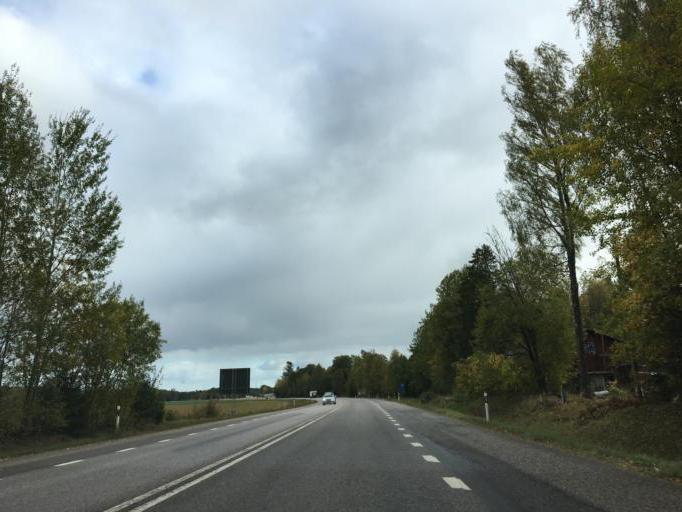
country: SE
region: Soedermanland
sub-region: Nykopings Kommun
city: Svalsta
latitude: 58.7707
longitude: 16.9331
